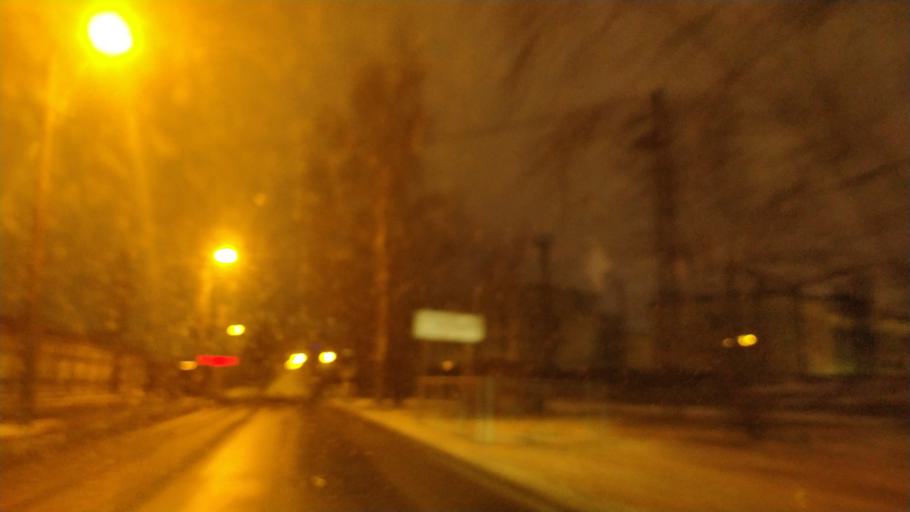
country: RU
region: St.-Petersburg
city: Kupchino
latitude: 59.8831
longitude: 30.3272
